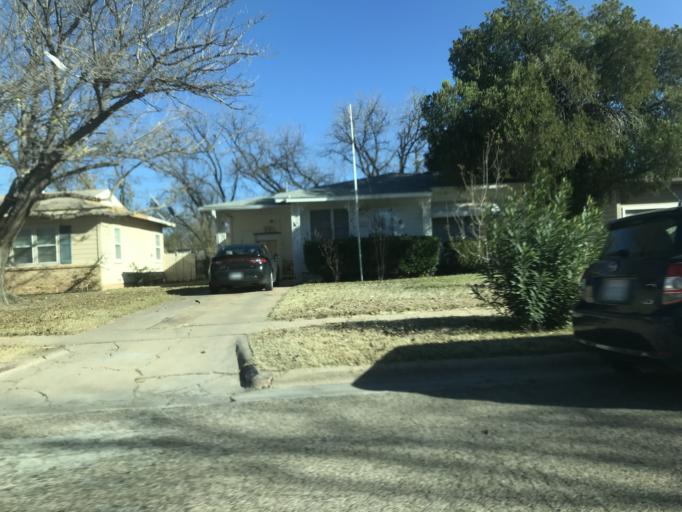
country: US
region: Texas
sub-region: Taylor County
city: Abilene
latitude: 32.4331
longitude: -99.7537
